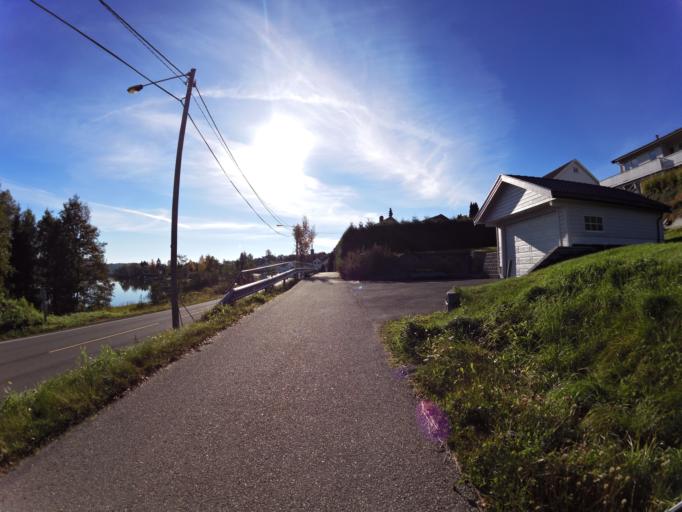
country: NO
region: Ostfold
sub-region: Fredrikstad
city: Fredrikstad
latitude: 59.2929
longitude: 10.9978
